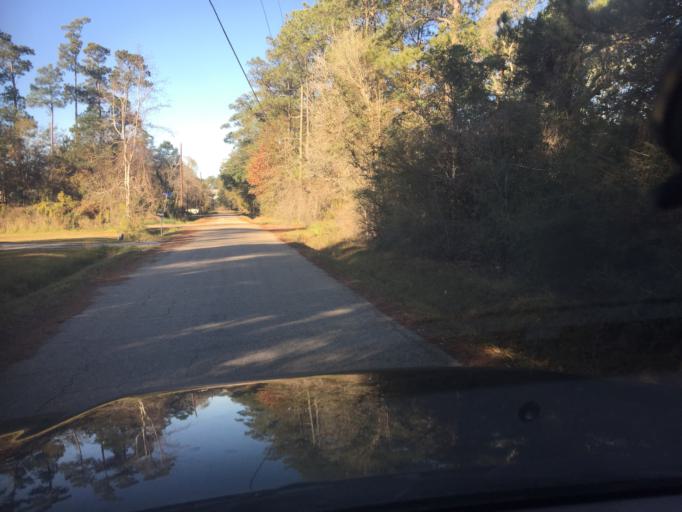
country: US
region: Louisiana
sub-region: Saint Tammany Parish
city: Slidell
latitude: 30.2439
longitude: -89.7678
